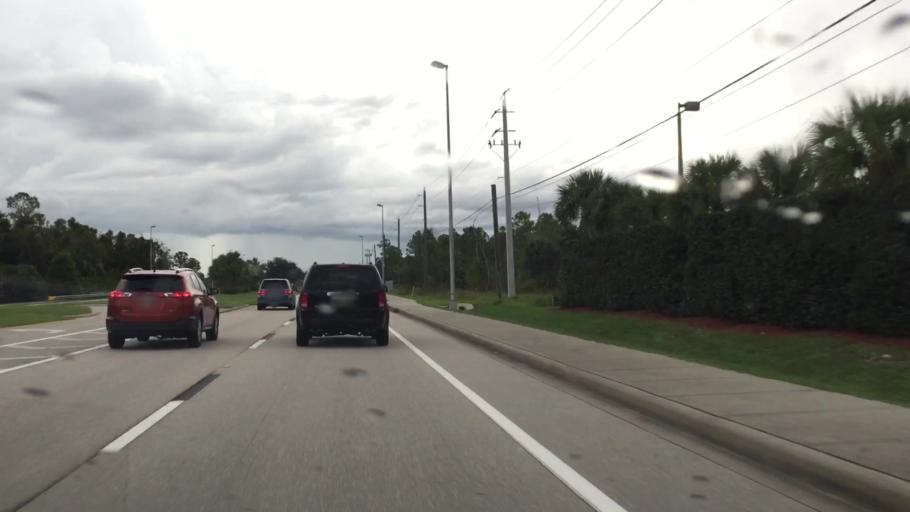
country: US
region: Florida
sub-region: Lee County
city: Estero
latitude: 26.4447
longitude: -81.7894
